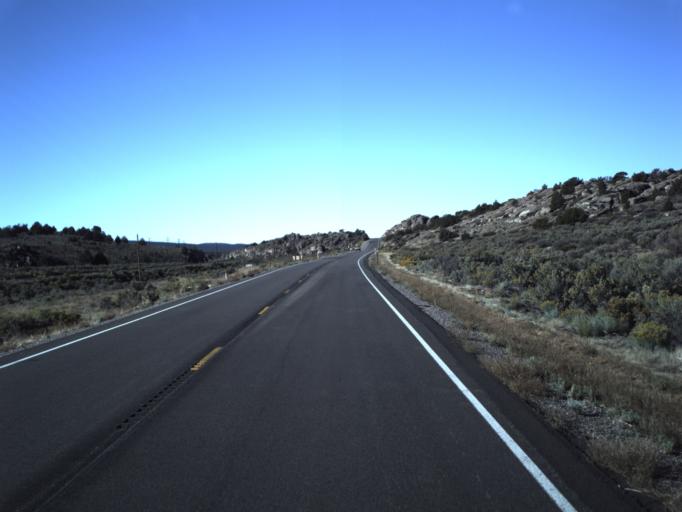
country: US
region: Utah
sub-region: Washington County
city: Enterprise
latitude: 37.7348
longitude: -114.0222
